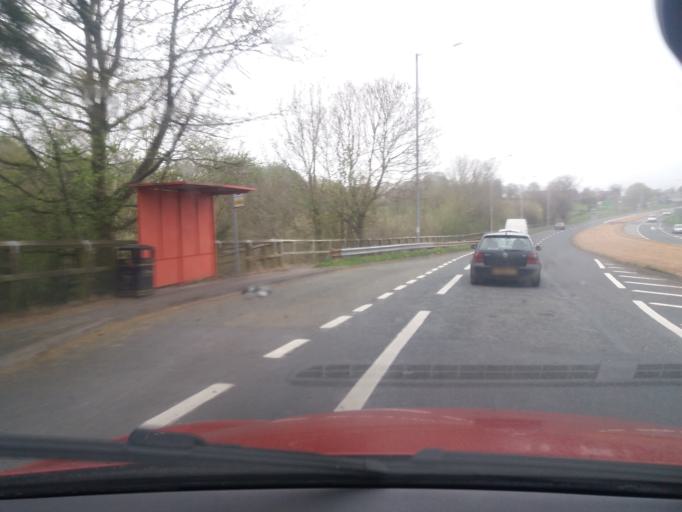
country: GB
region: England
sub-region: Lancashire
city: Chorley
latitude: 53.6792
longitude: -2.6168
